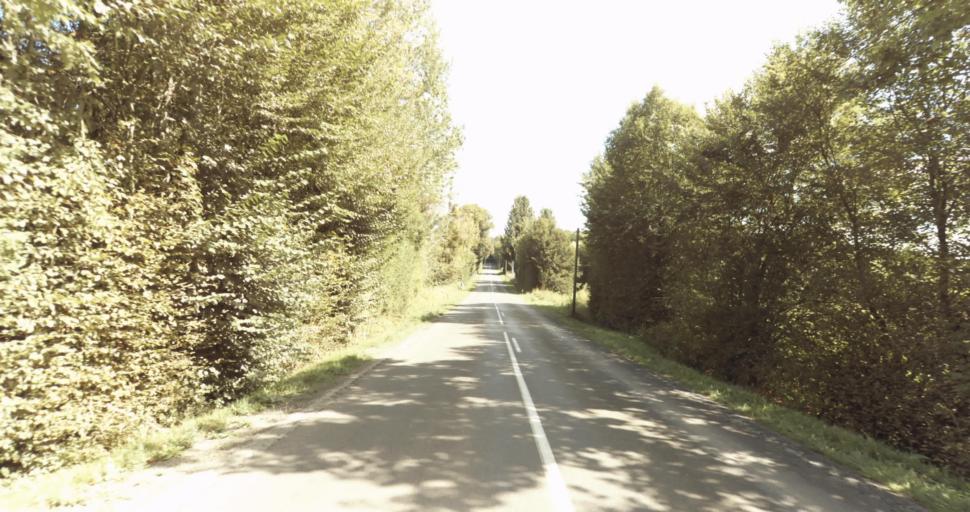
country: FR
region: Lower Normandy
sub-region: Departement de l'Orne
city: Vimoutiers
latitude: 48.9058
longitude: 0.2686
